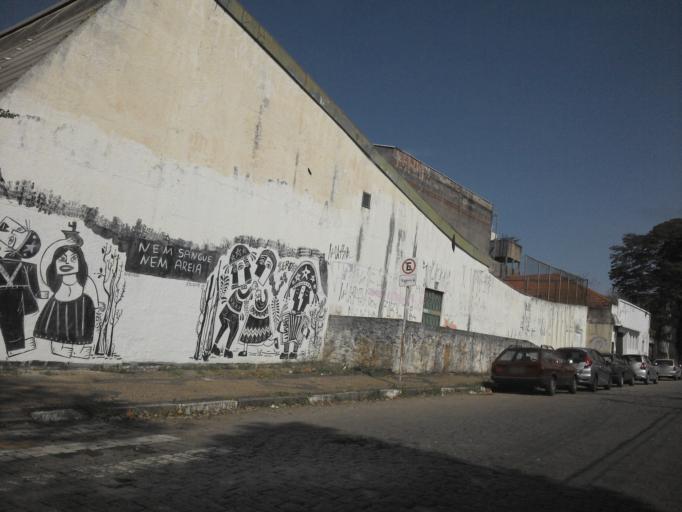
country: BR
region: Sao Paulo
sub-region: Campinas
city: Campinas
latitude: -22.9103
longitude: -47.0657
